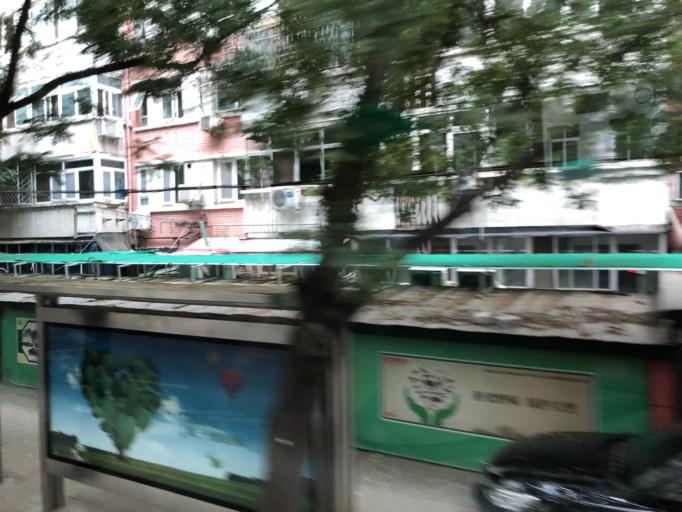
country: CN
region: Beijing
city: Jinrongjie
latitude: 39.9509
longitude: 116.3282
